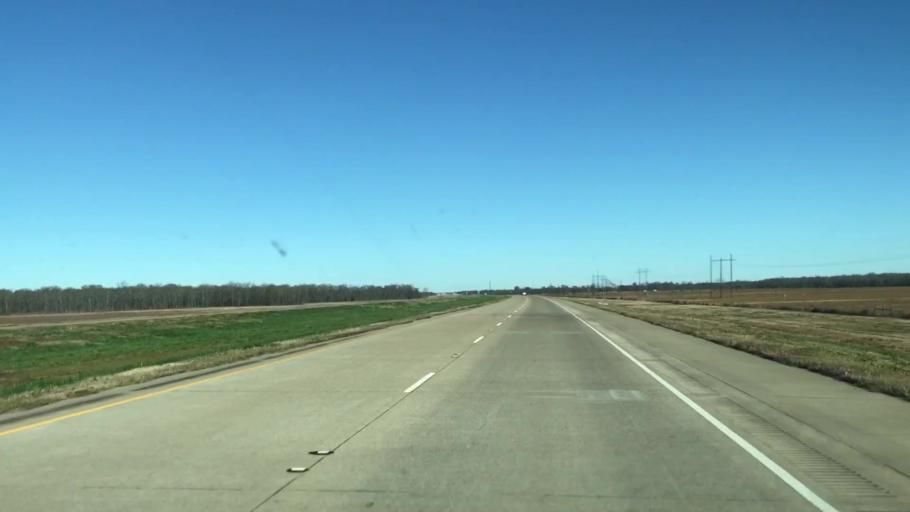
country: US
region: Louisiana
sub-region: Caddo Parish
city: Blanchard
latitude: 32.6502
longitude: -93.8406
